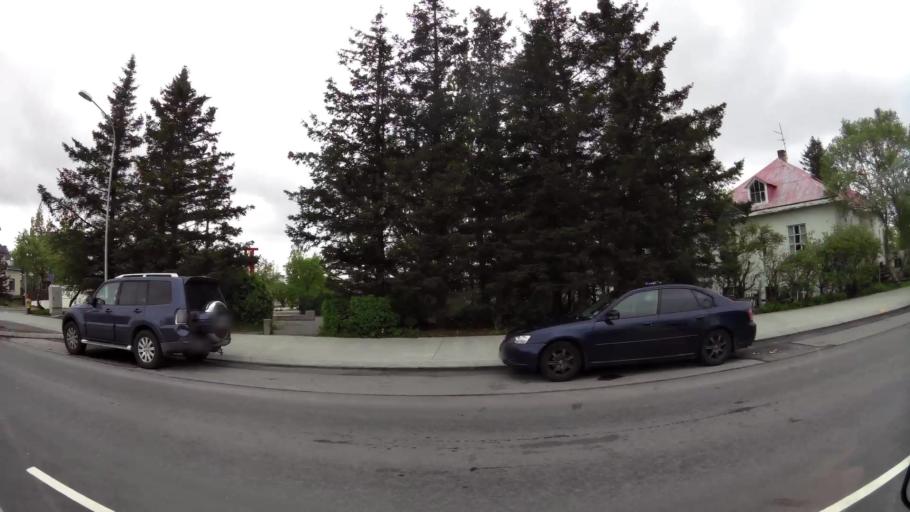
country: IS
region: Capital Region
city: Reykjavik
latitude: 64.1378
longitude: -21.8582
